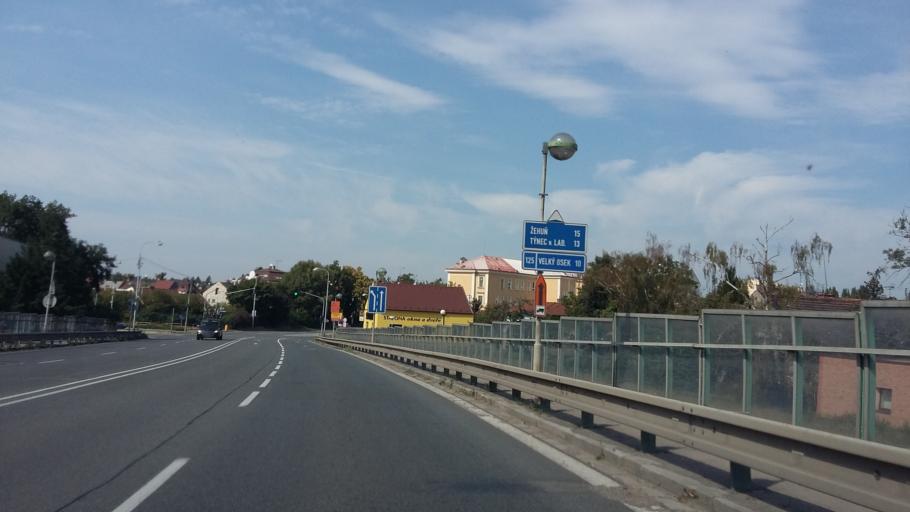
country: CZ
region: Central Bohemia
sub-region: Okres Kolin
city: Kolin
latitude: 50.0313
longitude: 15.2075
